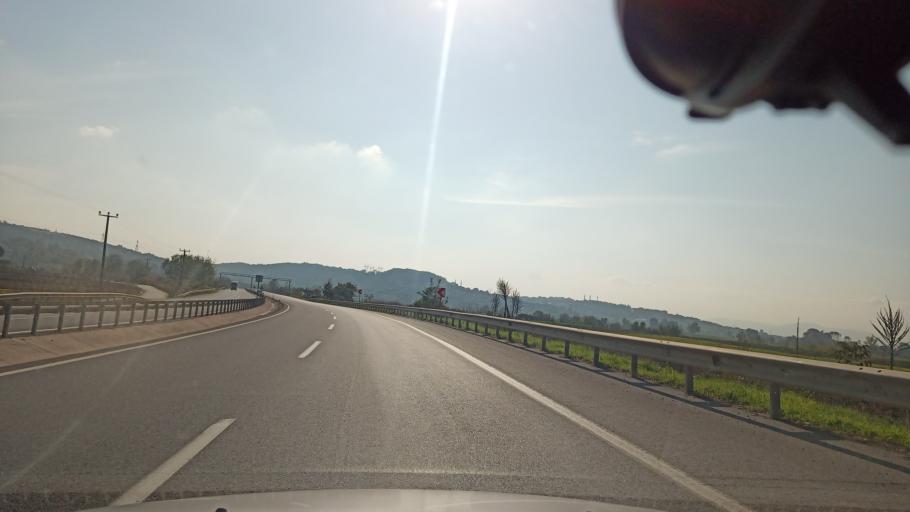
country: TR
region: Kocaeli
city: Kaymaz
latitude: 40.8790
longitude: 30.3463
